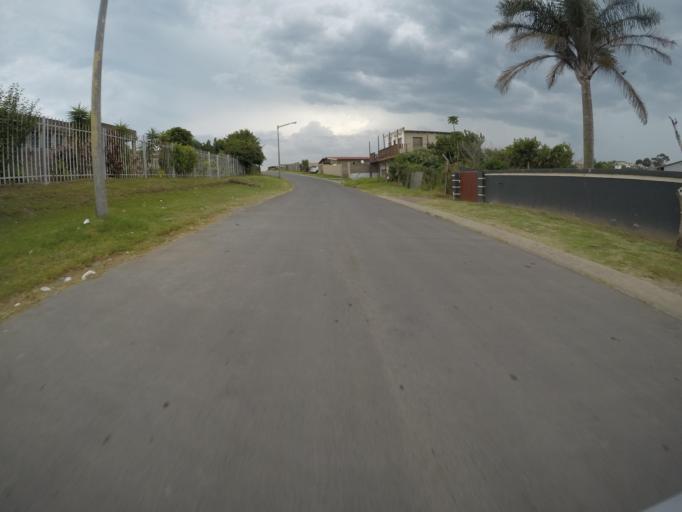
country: ZA
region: Eastern Cape
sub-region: Buffalo City Metropolitan Municipality
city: East London
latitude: -33.0199
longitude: 27.8684
